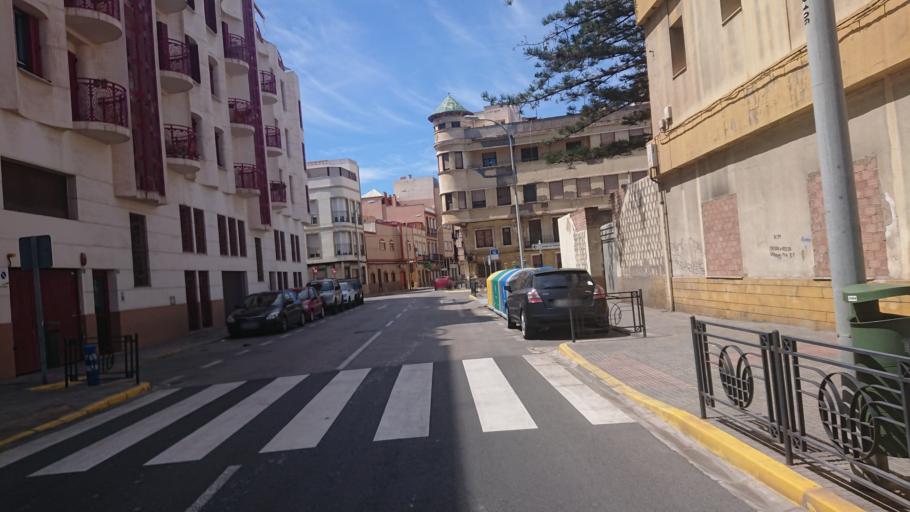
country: ES
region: Melilla
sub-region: Melilla
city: Melilla
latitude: 35.2900
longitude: -2.9399
